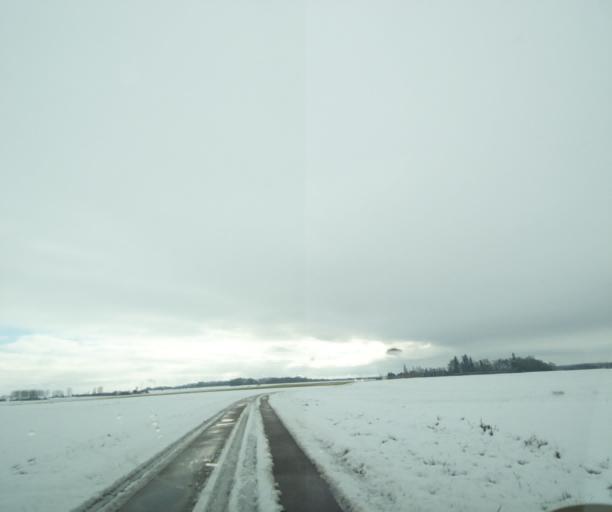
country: FR
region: Champagne-Ardenne
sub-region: Departement de la Haute-Marne
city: Montier-en-Der
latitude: 48.4616
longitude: 4.6506
